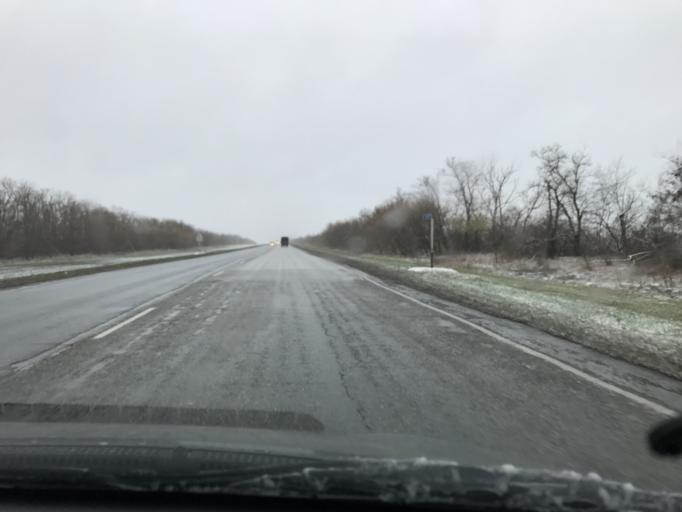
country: RU
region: Rostov
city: Mechetinskaya
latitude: 46.7342
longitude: 40.4758
